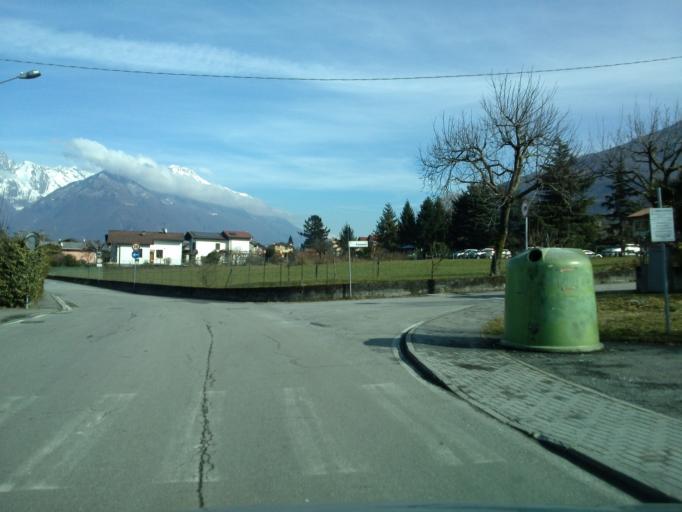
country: IT
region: Lombardy
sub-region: Provincia di Lecco
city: Colico Piano
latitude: 46.1278
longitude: 9.3657
